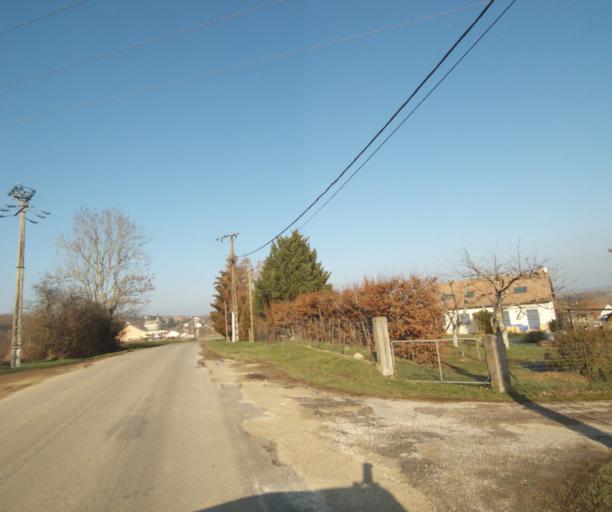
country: FR
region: Champagne-Ardenne
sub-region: Departement de la Haute-Marne
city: Wassy
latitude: 48.5092
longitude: 4.9211
